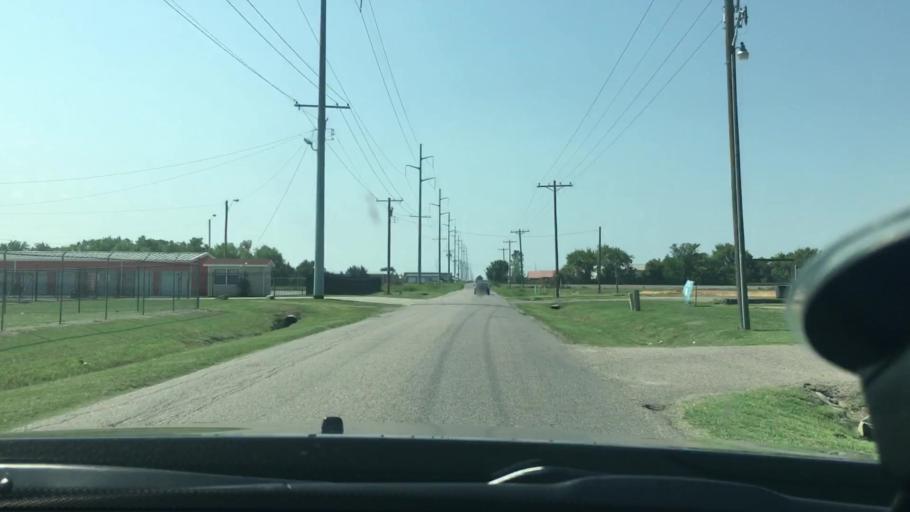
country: US
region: Oklahoma
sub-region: Bryan County
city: Durant
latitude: 34.0040
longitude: -96.4253
